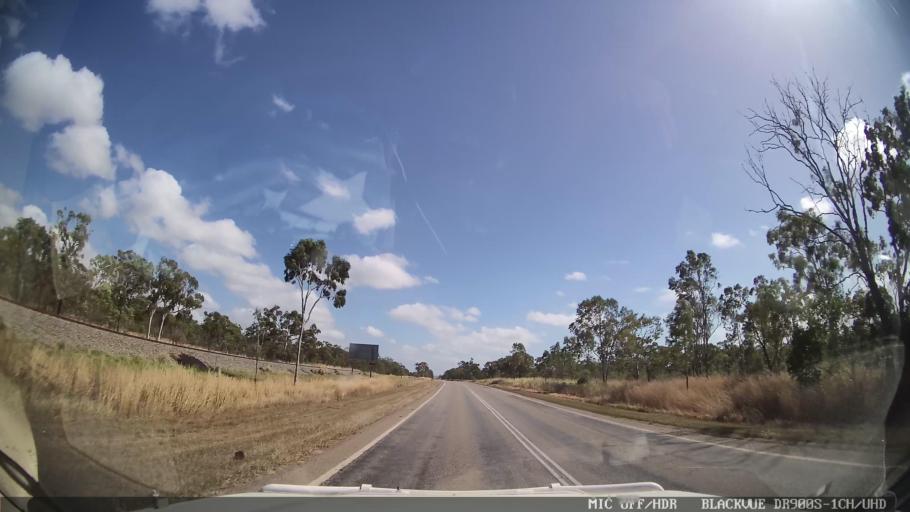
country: AU
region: Queensland
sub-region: Whitsunday
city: Bowen
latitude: -20.1773
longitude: 148.3468
